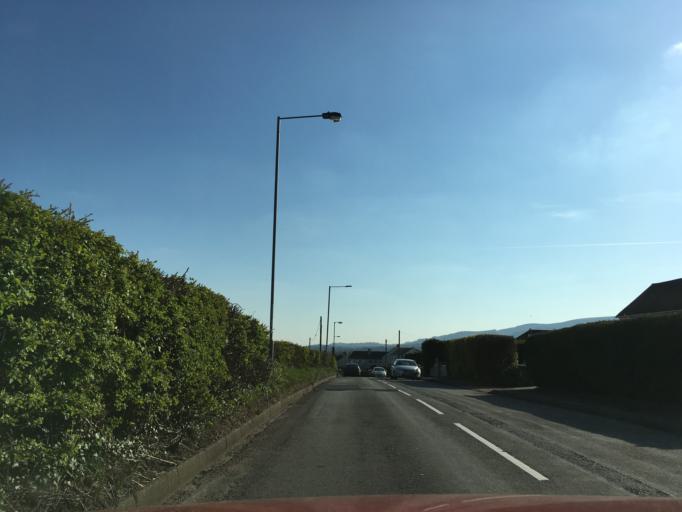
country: GB
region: Wales
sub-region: Torfaen County Borough
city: New Inn
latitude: 51.6900
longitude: -3.0026
